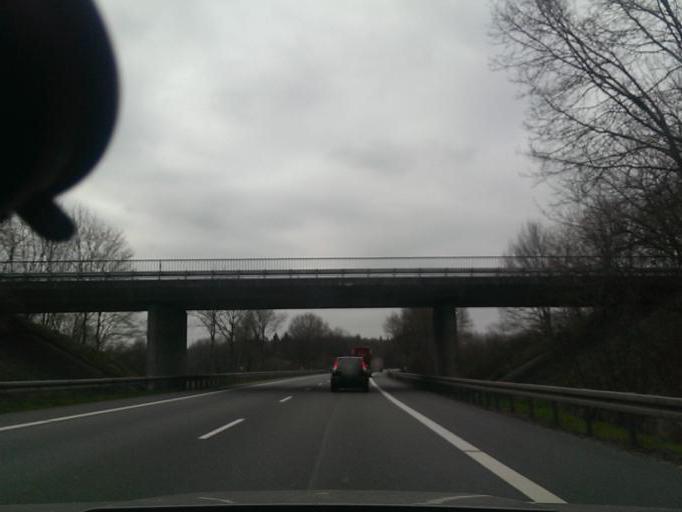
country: DE
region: North Rhine-Westphalia
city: Rietberg
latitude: 51.7958
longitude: 8.4163
